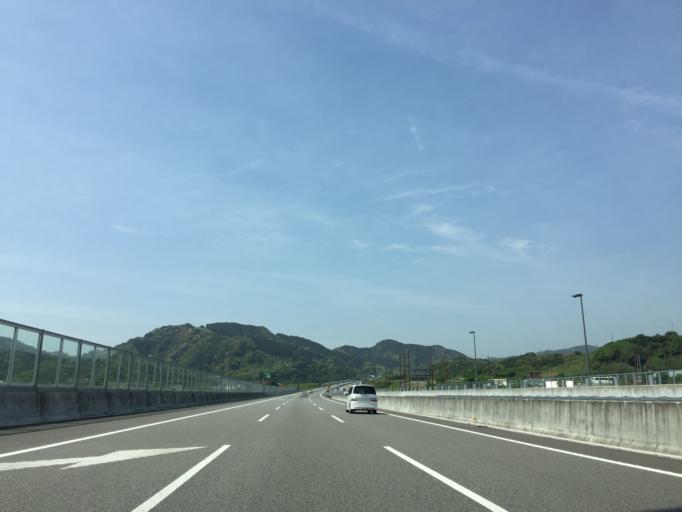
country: JP
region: Shizuoka
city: Fujieda
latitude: 34.9032
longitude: 138.2472
